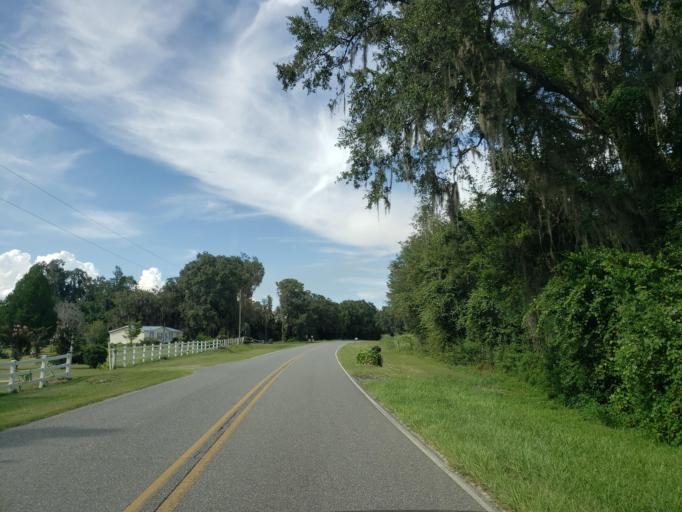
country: US
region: Georgia
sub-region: Echols County
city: Statenville
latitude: 30.6035
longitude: -83.2223
